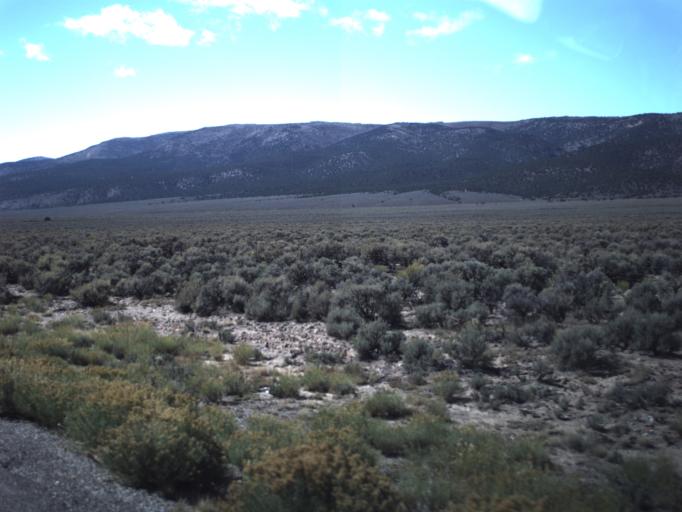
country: US
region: Utah
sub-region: Piute County
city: Junction
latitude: 38.2787
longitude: -111.9831
